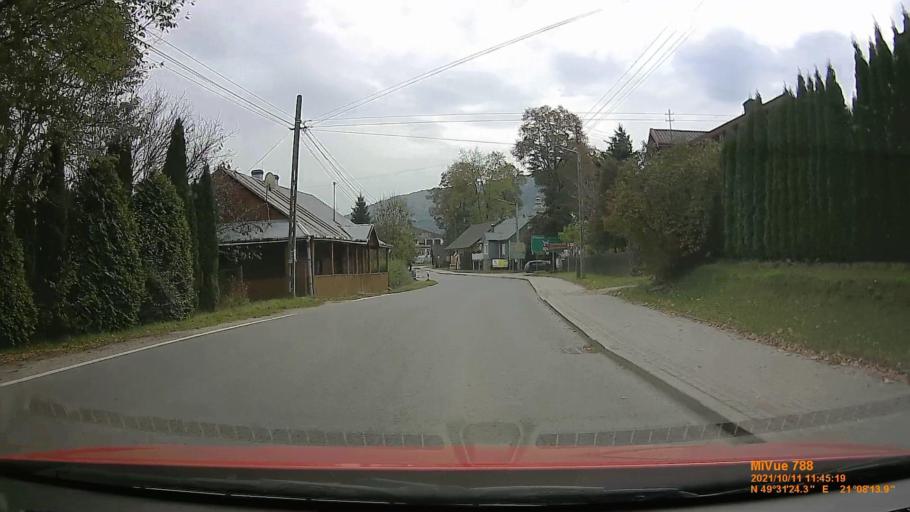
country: PL
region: Lesser Poland Voivodeship
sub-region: Powiat gorlicki
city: Uscie Gorlickie
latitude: 49.5232
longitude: 21.1373
